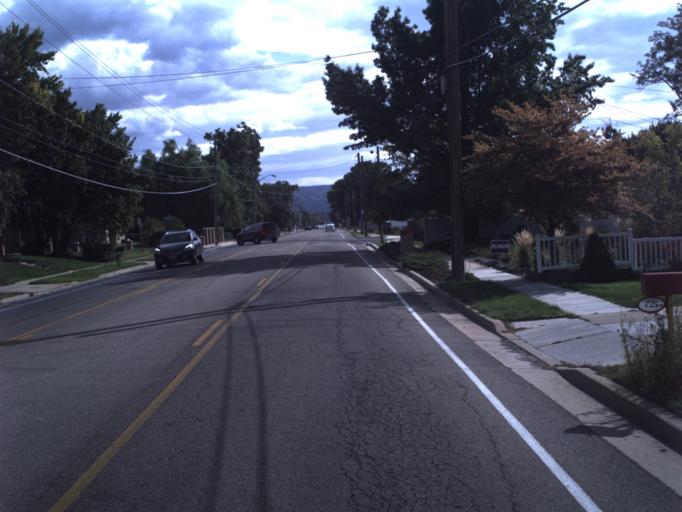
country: US
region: Utah
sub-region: Davis County
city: Centerville
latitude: 40.9256
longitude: -111.8790
